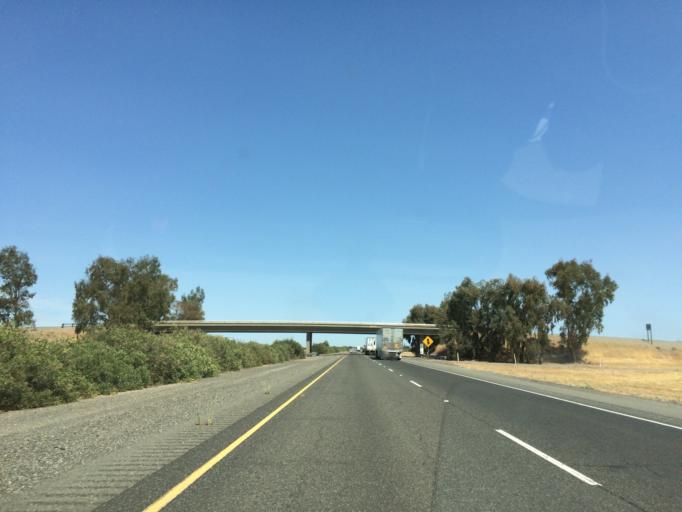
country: US
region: California
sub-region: Glenn County
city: Willows
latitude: 39.6227
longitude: -122.2054
